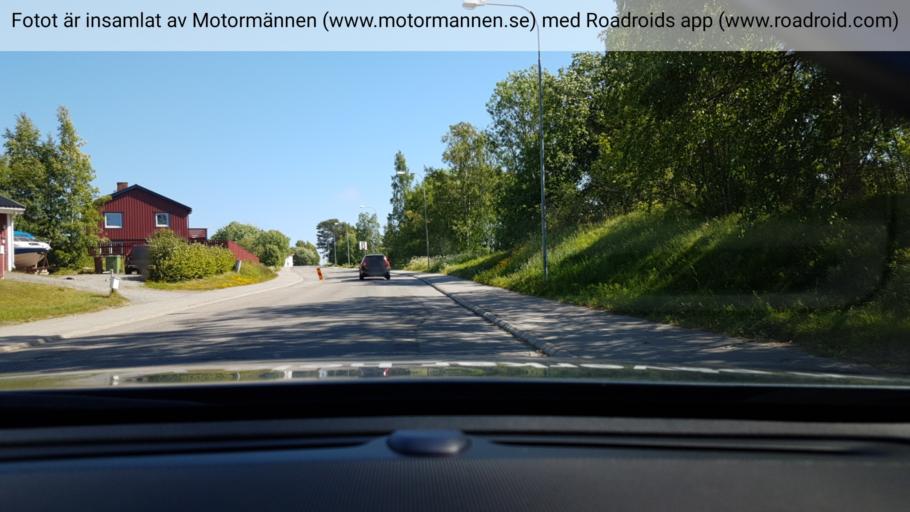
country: SE
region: Vaesterbotten
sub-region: Umea Kommun
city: Holmsund
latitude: 63.7115
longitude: 20.3737
